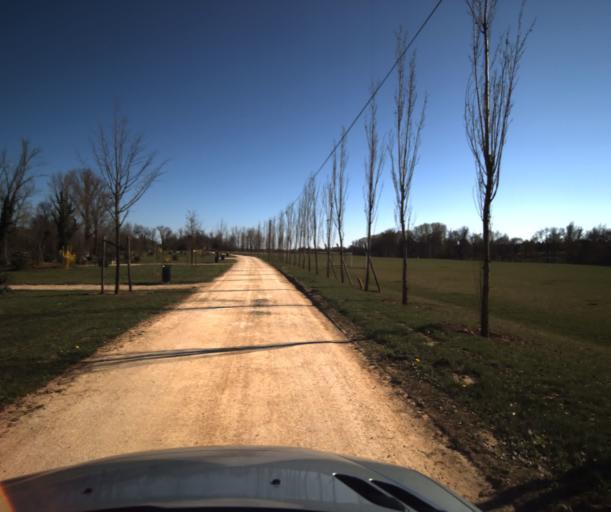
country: FR
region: Midi-Pyrenees
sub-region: Departement du Tarn-et-Garonne
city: Bressols
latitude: 43.9652
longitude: 1.3436
